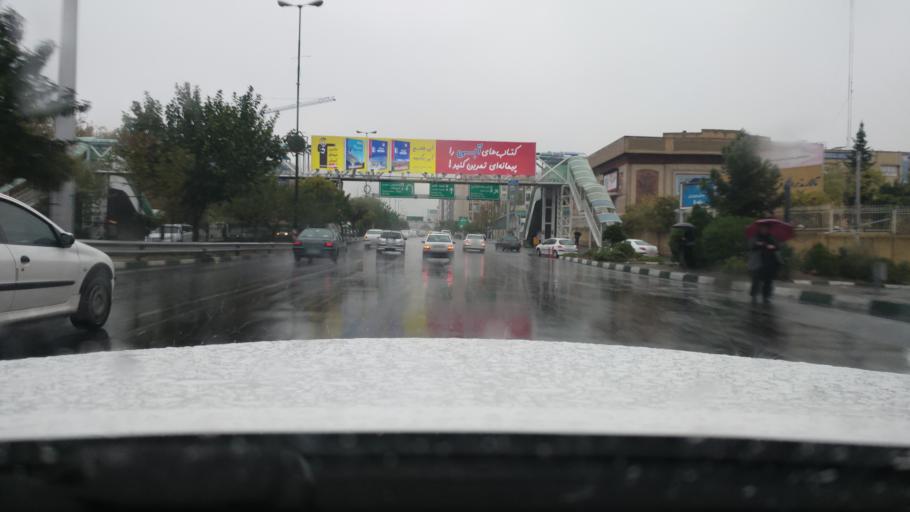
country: IR
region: Tehran
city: Tehran
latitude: 35.7251
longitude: 51.3094
